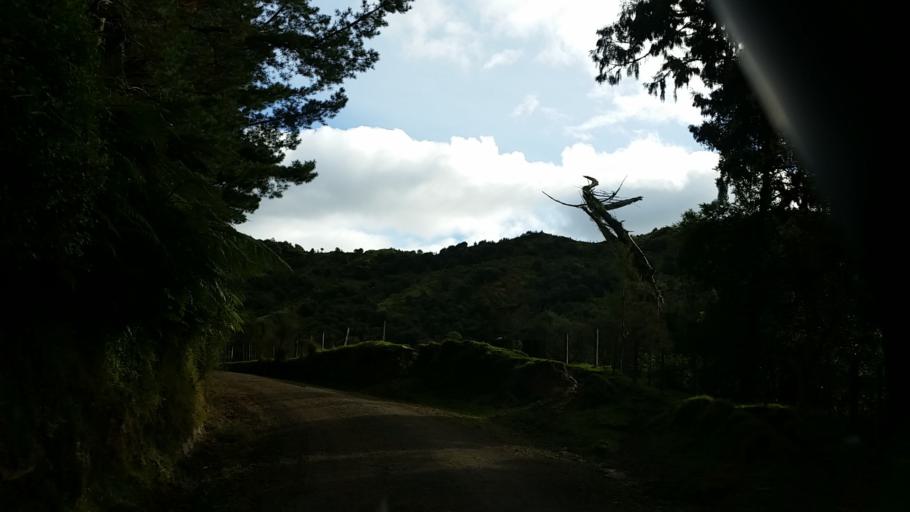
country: NZ
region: Taranaki
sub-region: New Plymouth District
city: Waitara
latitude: -39.0684
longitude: 174.5604
